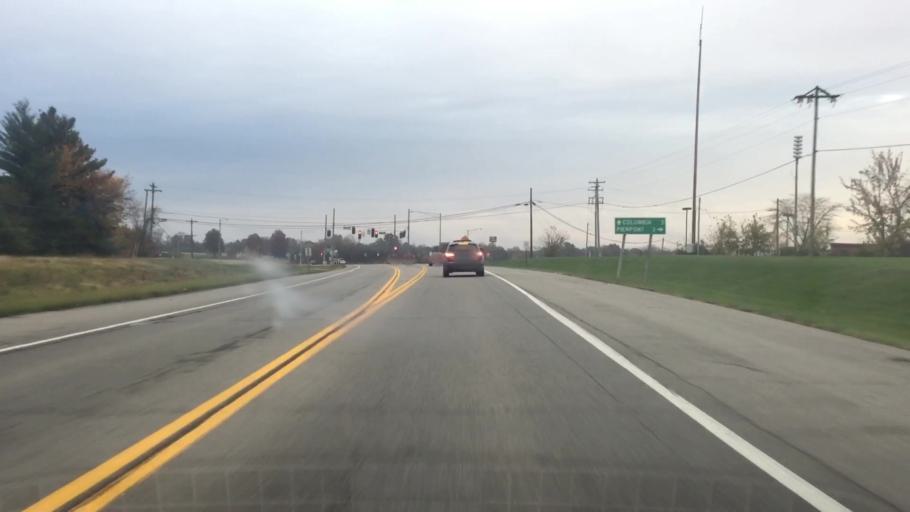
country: US
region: Missouri
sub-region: Boone County
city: Columbia
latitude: 38.8909
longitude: -92.3372
